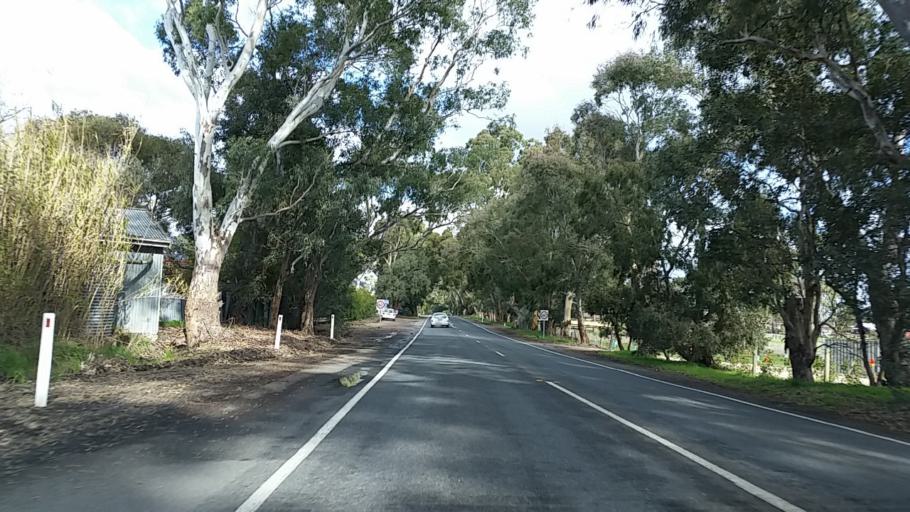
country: AU
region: South Australia
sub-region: Mount Barker
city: Hahndorf
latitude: -35.1000
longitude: 138.7931
